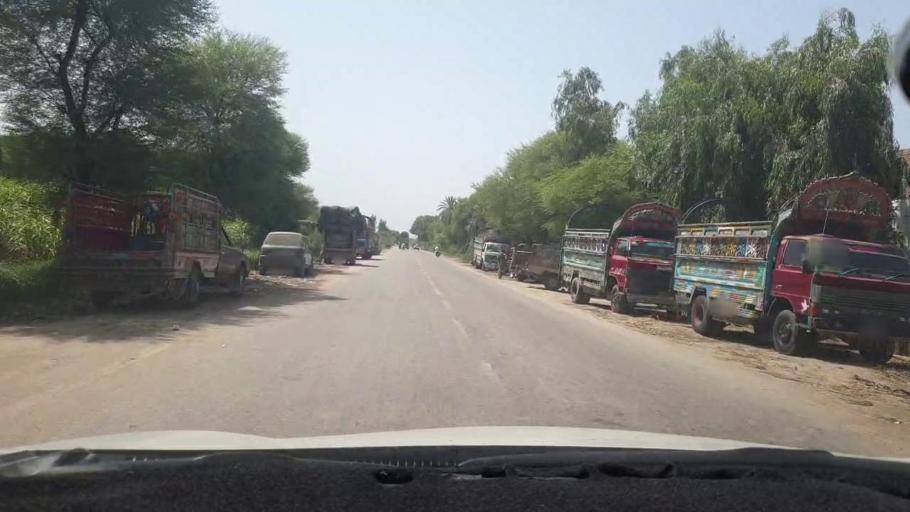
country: PK
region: Sindh
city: Bhit Shah
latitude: 25.8754
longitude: 68.5456
